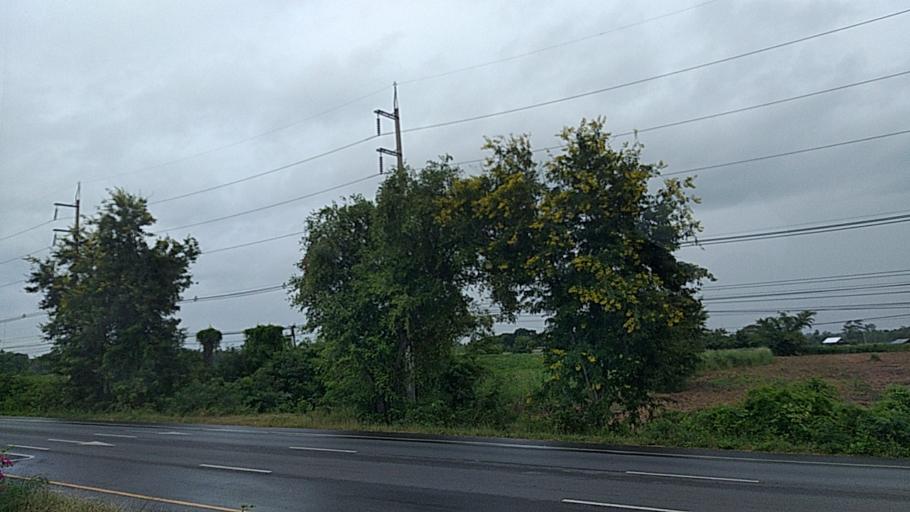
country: TH
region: Maha Sarakham
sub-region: Amphoe Borabue
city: Borabue
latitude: 16.0597
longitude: 103.1375
